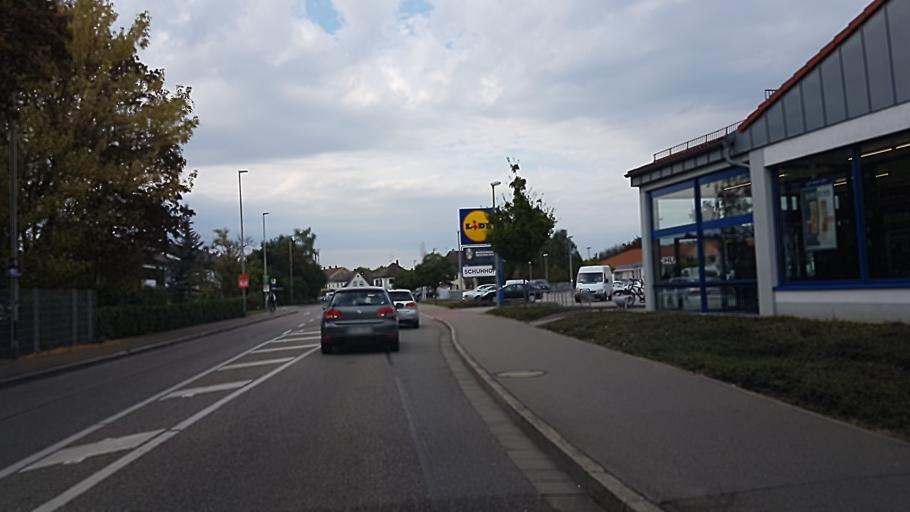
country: DE
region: Baden-Wuerttemberg
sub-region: Freiburg Region
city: Emmendingen
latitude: 48.1111
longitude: 7.8656
